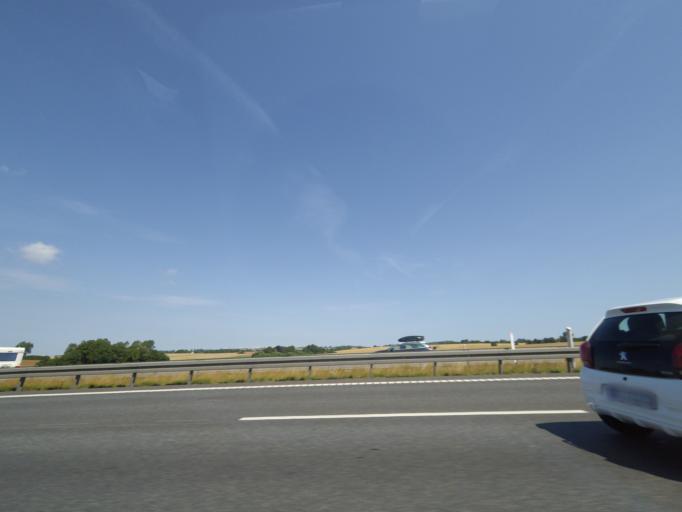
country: DK
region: South Denmark
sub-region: Middelfart Kommune
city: Strib
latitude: 55.4931
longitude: 9.8159
